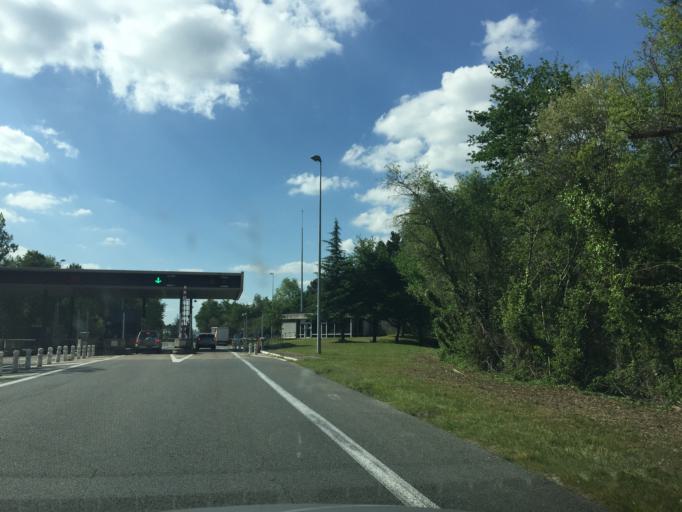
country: FR
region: Aquitaine
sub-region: Departement de la Gironde
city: La Reole
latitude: 44.5111
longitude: -0.0489
